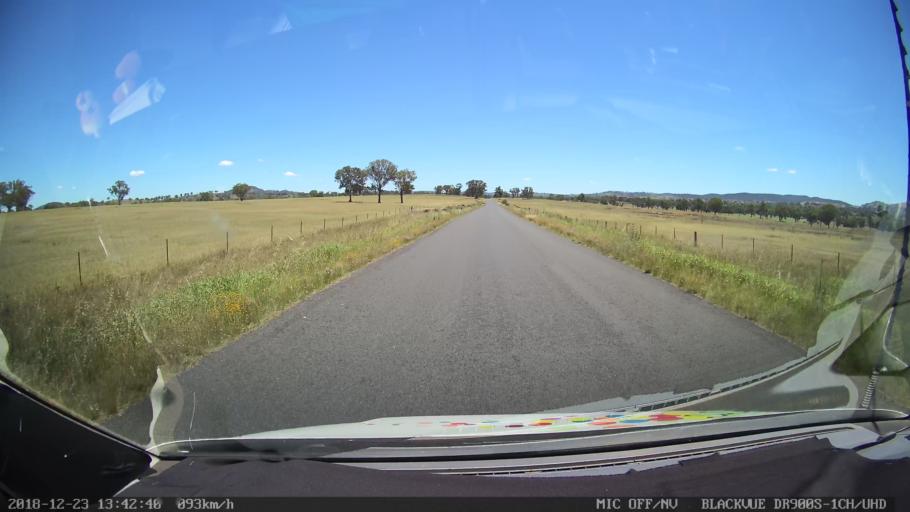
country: AU
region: New South Wales
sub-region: Armidale Dumaresq
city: Armidale
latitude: -30.4794
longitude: 151.1601
